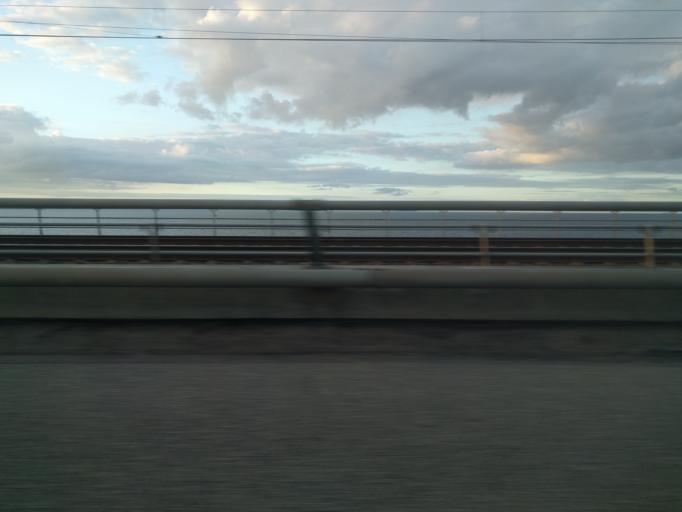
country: DK
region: Zealand
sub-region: Slagelse Kommune
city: Korsor
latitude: 55.3355
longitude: 10.9934
